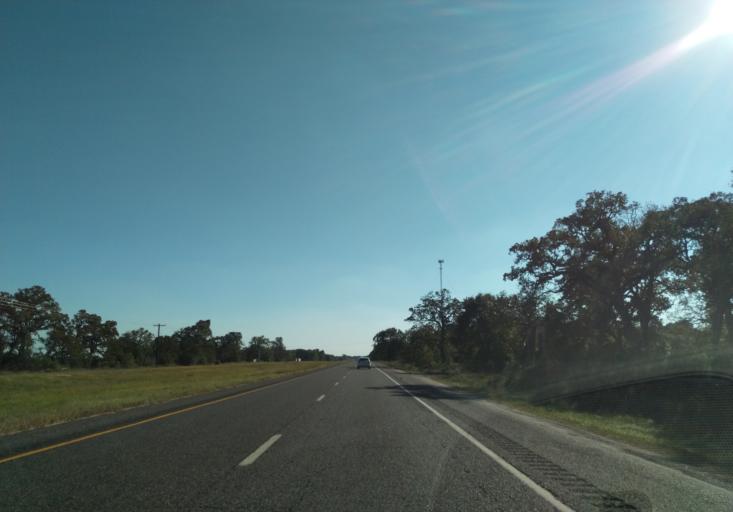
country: US
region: Texas
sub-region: Waller County
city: Hempstead
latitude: 30.1355
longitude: -96.0724
